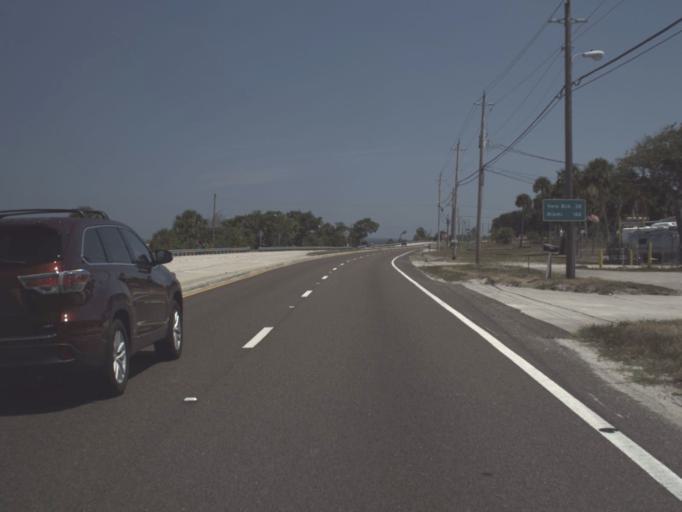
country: US
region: Florida
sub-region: Brevard County
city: Malabar
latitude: 28.0037
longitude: -80.5633
